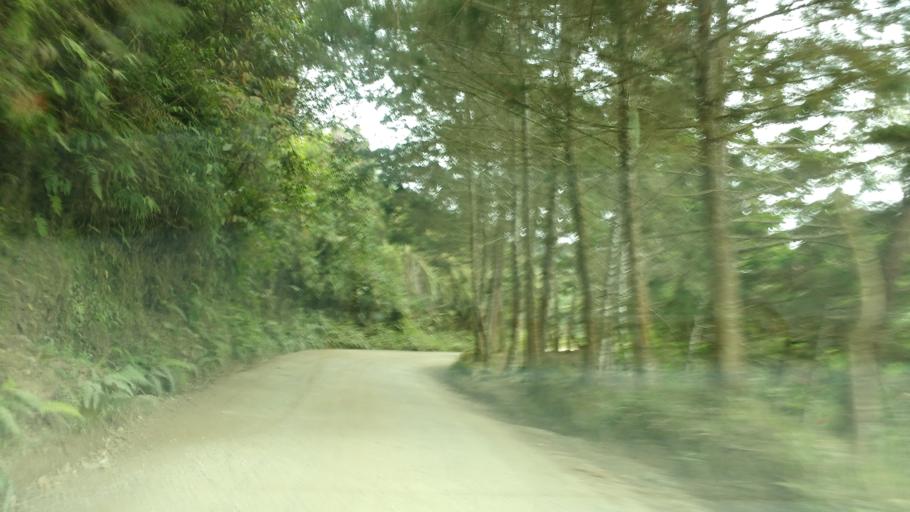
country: CO
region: Antioquia
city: Concepcion
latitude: 6.3327
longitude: -75.2834
